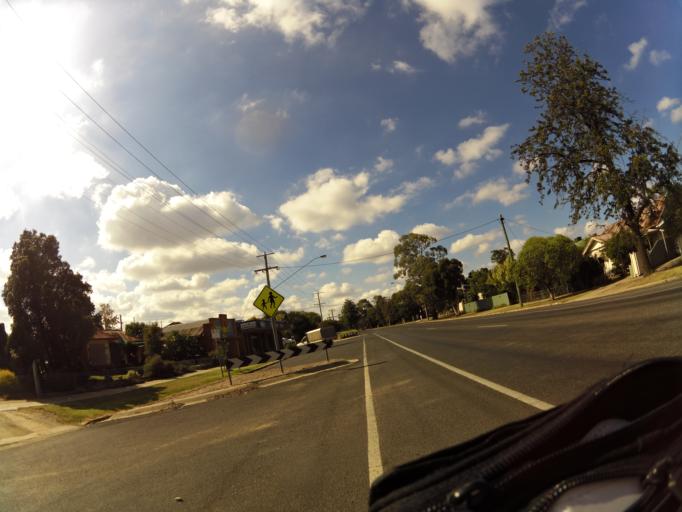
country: AU
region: Victoria
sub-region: Benalla
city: Benalla
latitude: -36.5537
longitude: 145.9905
